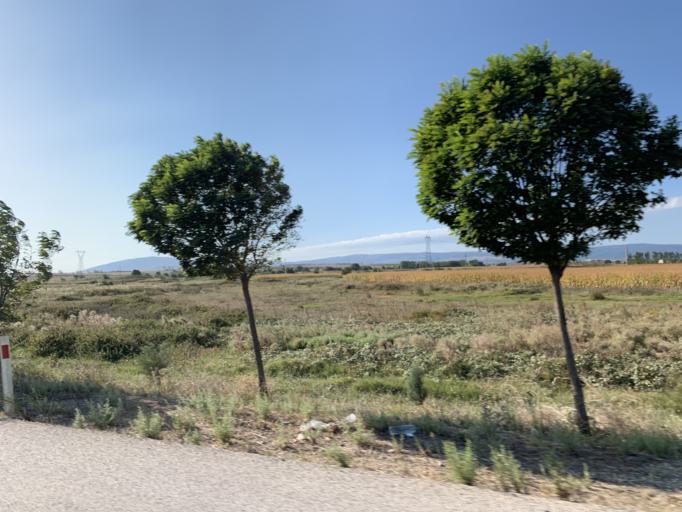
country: TR
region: Bursa
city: Karacabey
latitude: 40.2306
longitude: 28.4654
